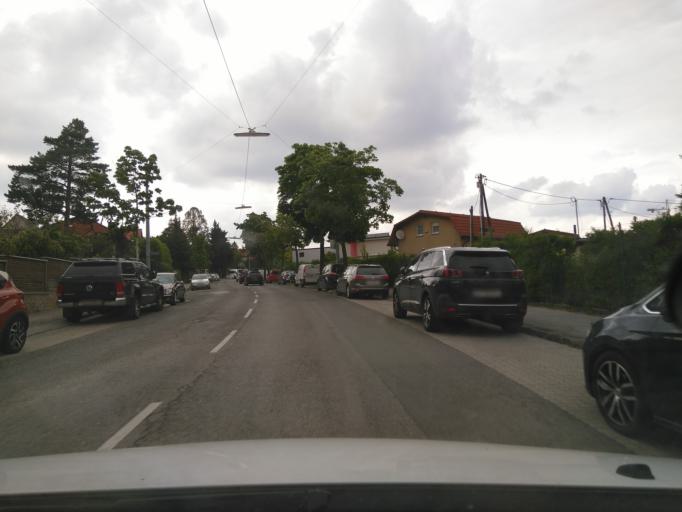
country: AT
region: Lower Austria
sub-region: Politischer Bezirk Modling
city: Perchtoldsdorf
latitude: 48.1554
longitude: 16.2916
